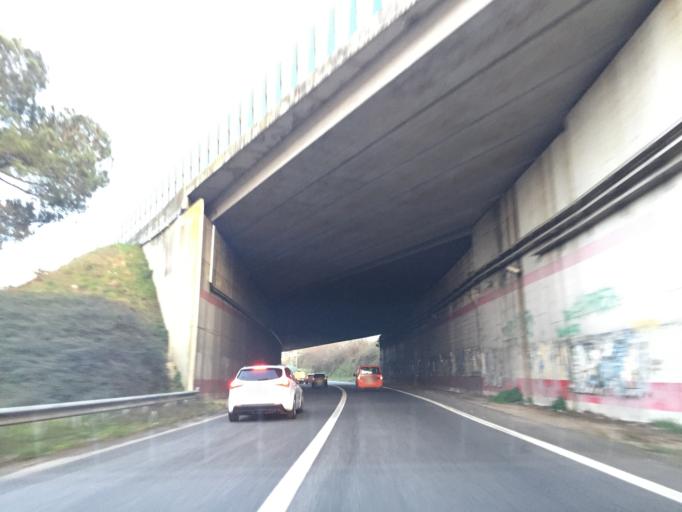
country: IT
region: Latium
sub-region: Citta metropolitana di Roma Capitale
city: Monte Caminetto
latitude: 41.9864
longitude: 12.4745
